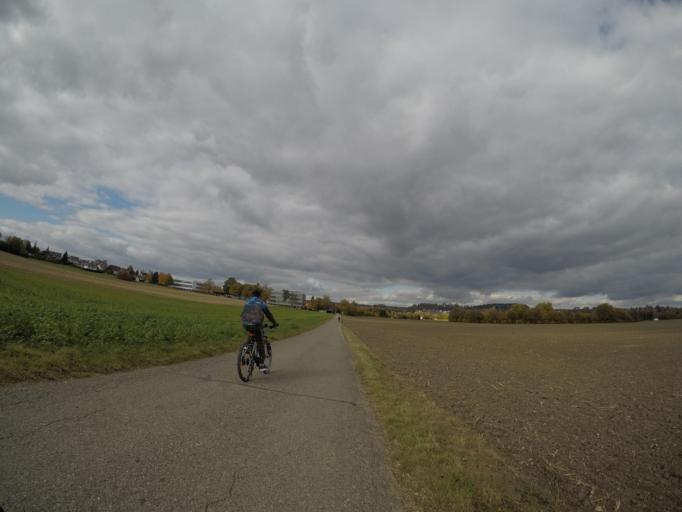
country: DE
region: Baden-Wuerttemberg
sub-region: Tuebingen Region
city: Munderkingen
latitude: 48.2276
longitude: 9.6506
